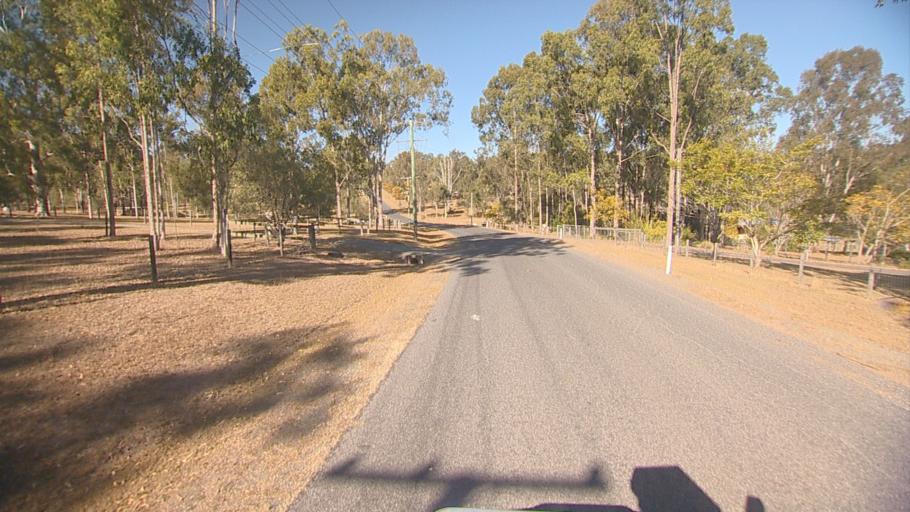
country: AU
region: Queensland
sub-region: Logan
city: Cedar Vale
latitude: -27.8694
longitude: 152.9831
